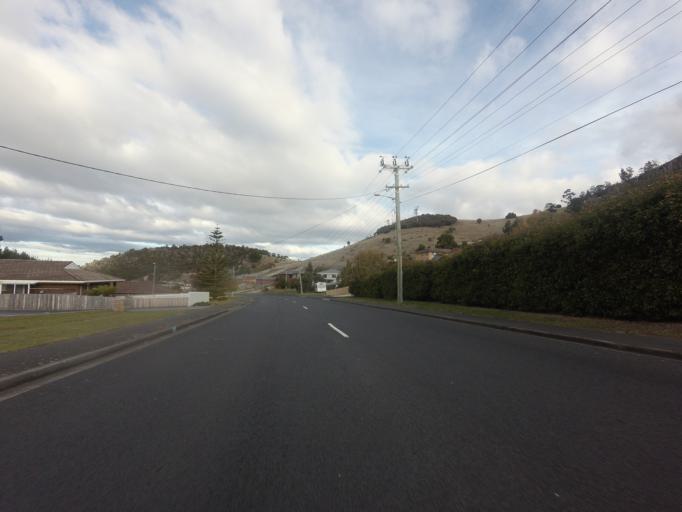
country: AU
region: Tasmania
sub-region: Glenorchy
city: Berriedale
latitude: -42.8221
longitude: 147.2473
